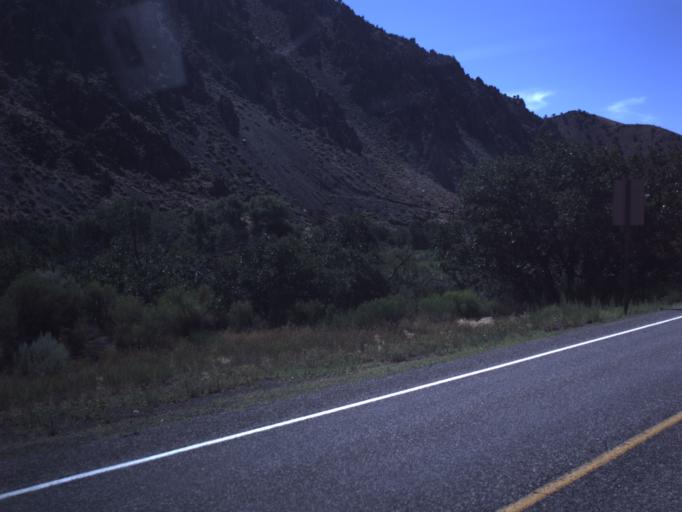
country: US
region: Utah
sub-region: Sevier County
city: Monroe
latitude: 38.5083
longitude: -112.2597
